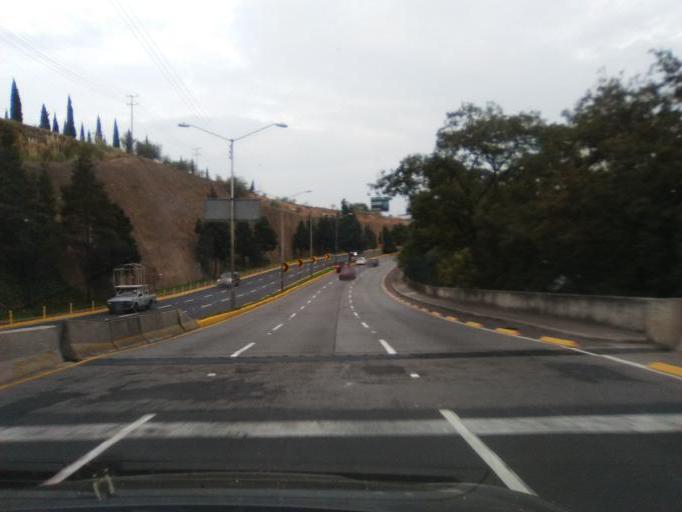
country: MX
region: Mexico City
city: Col. Bosques de las Lomas
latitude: 19.3525
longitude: -99.2595
